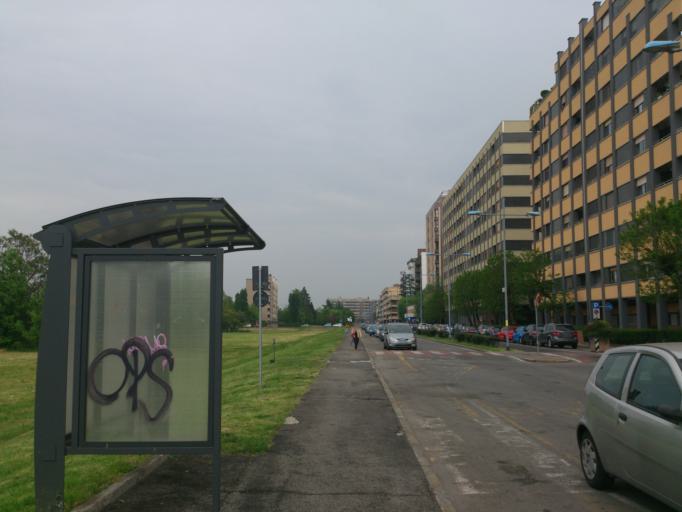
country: IT
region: Lombardy
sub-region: Citta metropolitana di Milano
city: San Donato Milanese
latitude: 45.4151
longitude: 9.2662
